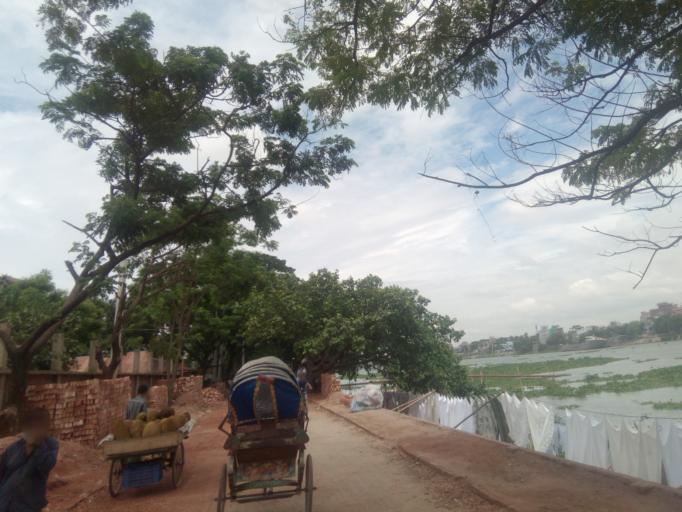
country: BD
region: Dhaka
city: Azimpur
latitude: 23.7083
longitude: 90.3700
